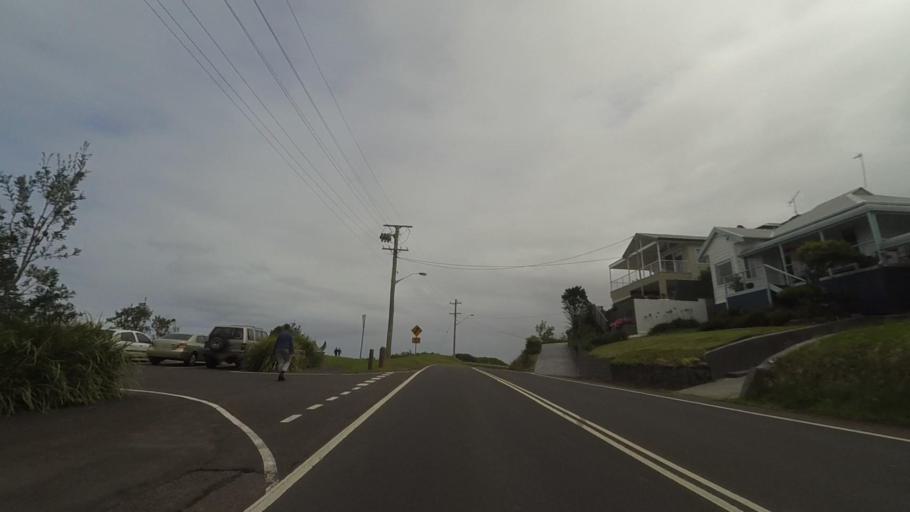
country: AU
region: New South Wales
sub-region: Wollongong
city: Bulli
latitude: -34.2847
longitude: 150.9505
